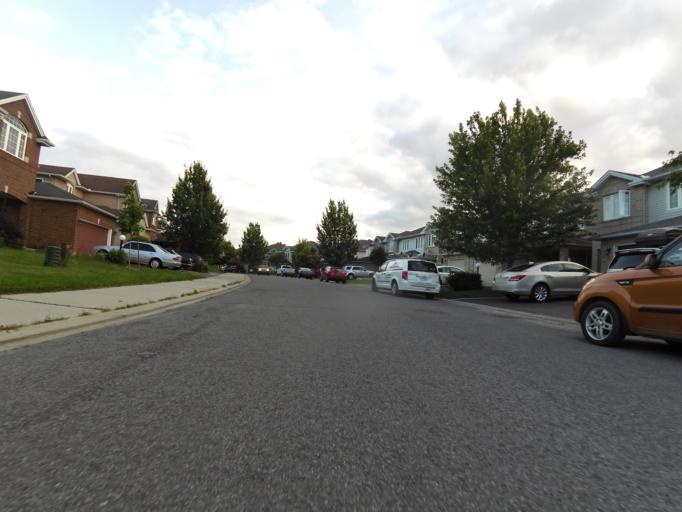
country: CA
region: Ontario
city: Bells Corners
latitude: 45.2829
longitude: -75.7374
